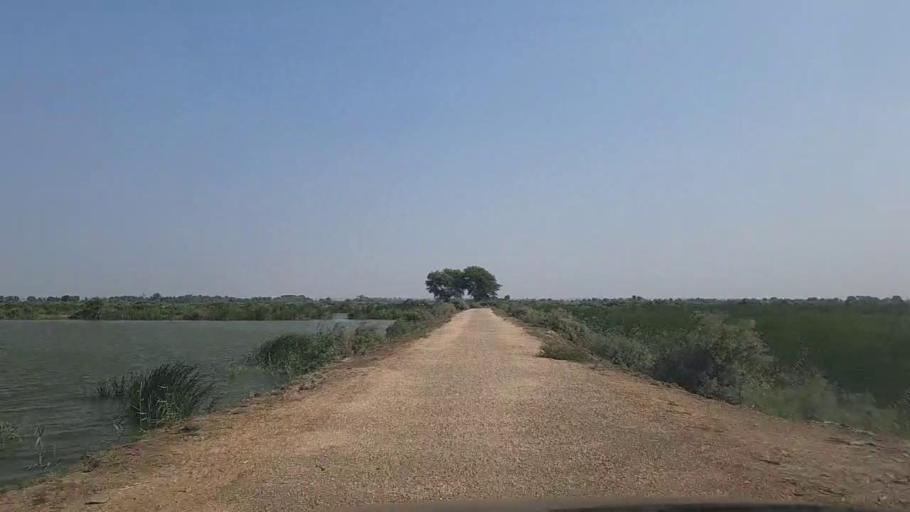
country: PK
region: Sindh
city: Thatta
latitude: 24.6230
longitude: 67.7925
